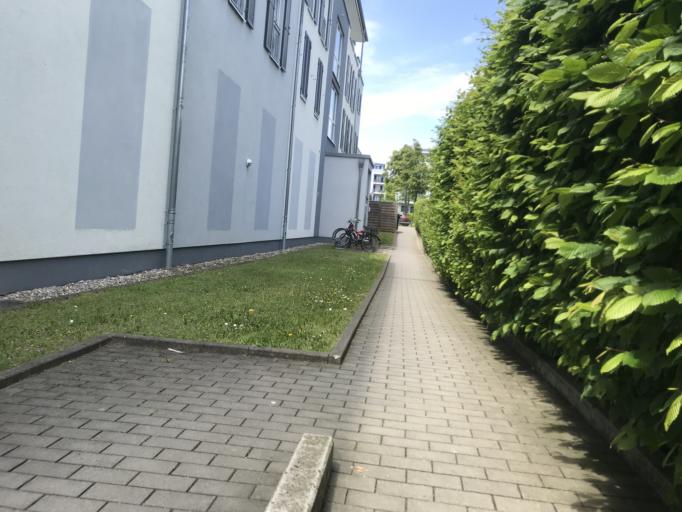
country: DE
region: Hesse
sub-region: Regierungsbezirk Darmstadt
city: Bad Homburg vor der Hoehe
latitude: 50.1762
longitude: 8.6424
